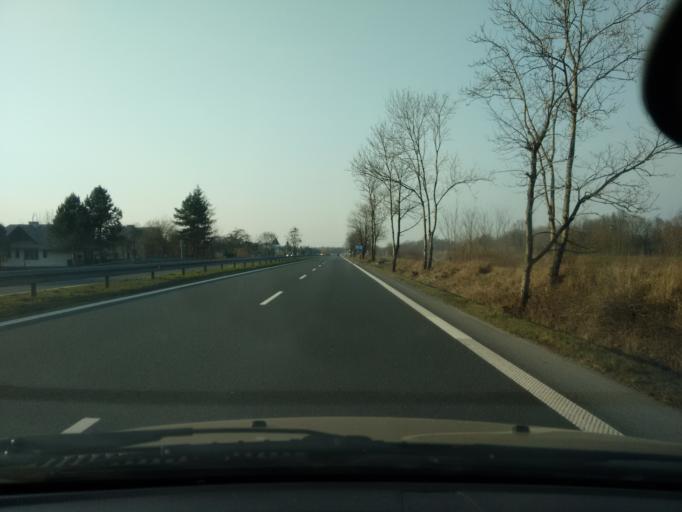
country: PL
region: Silesian Voivodeship
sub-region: Powiat cieszynski
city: Ochaby
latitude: 49.8375
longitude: 18.7735
